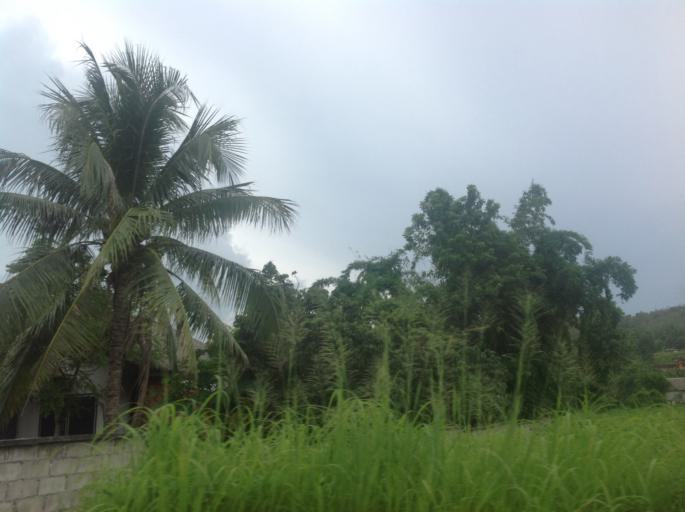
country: TH
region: Chiang Mai
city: Hang Dong
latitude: 18.6914
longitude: 98.8725
